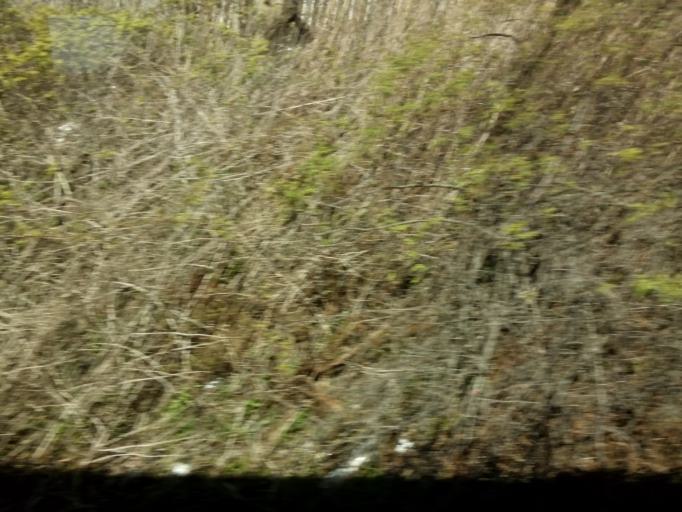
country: GB
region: Scotland
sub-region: Fife
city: Kirkcaldy
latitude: 56.1285
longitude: -3.1248
